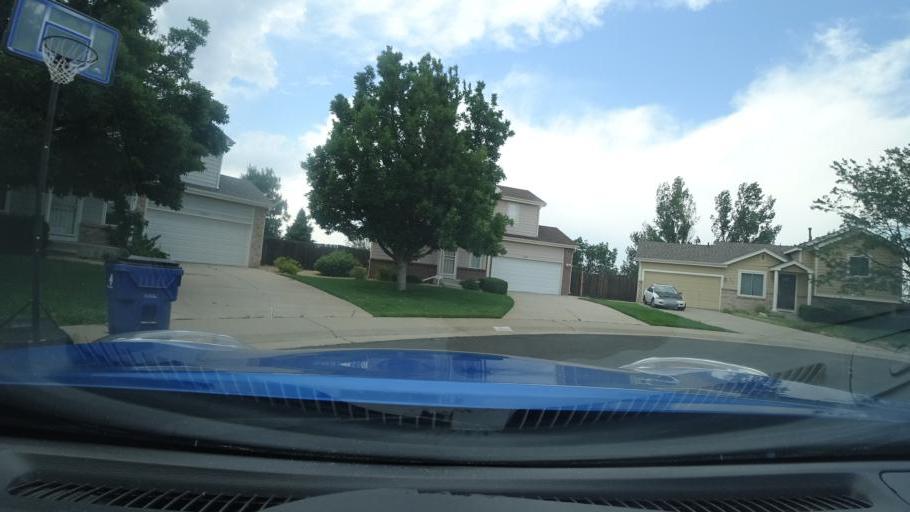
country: US
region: Colorado
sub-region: Adams County
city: Aurora
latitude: 39.6902
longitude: -104.7894
